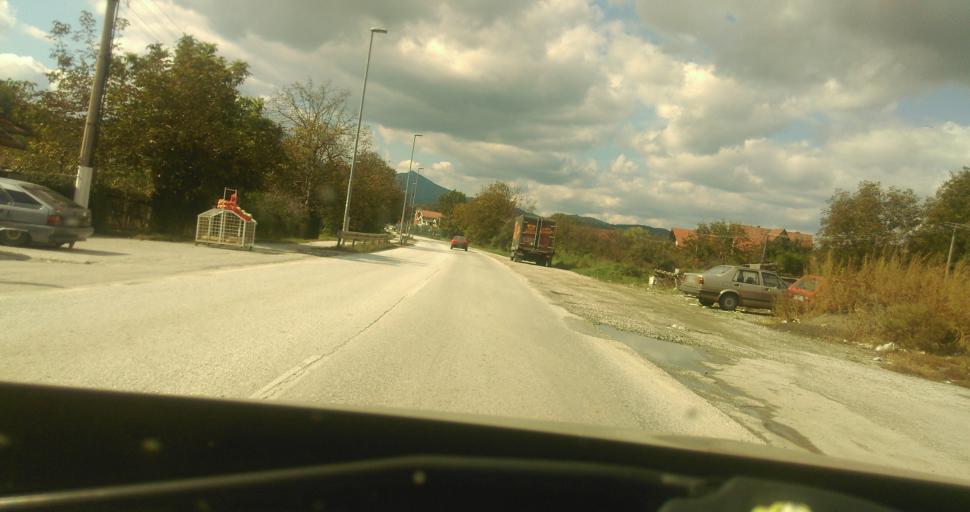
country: RS
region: Central Serbia
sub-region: Moravicki Okrug
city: Cacak
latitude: 43.8958
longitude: 20.2966
